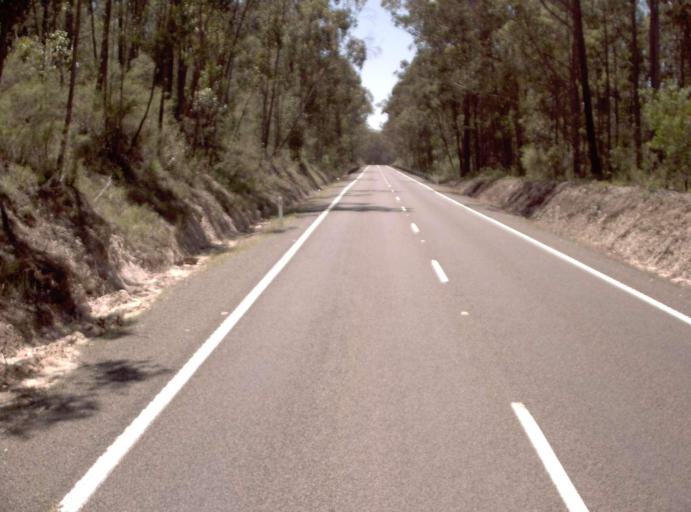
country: AU
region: Victoria
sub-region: East Gippsland
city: Lakes Entrance
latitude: -37.7623
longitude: 148.0596
